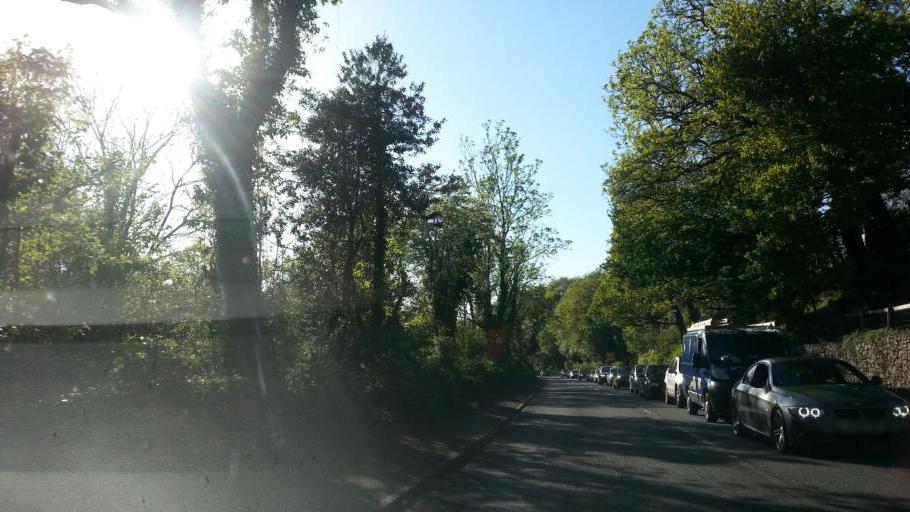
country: GB
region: England
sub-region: Bath and North East Somerset
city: Publow
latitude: 51.3642
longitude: -2.5448
